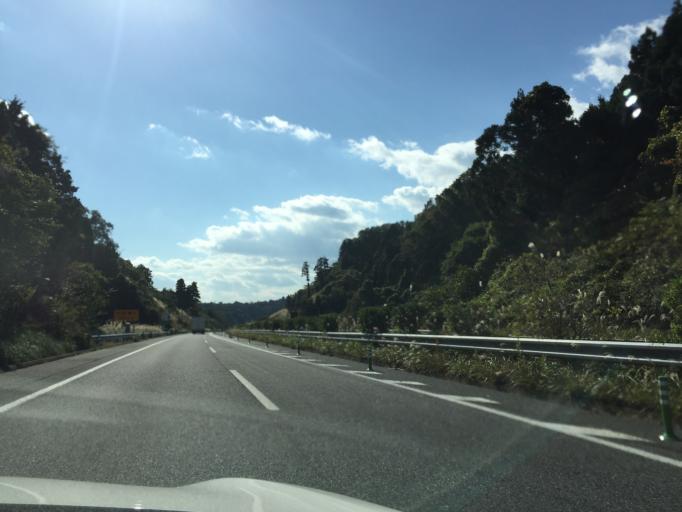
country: JP
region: Fukushima
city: Iwaki
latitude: 37.1862
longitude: 140.9839
